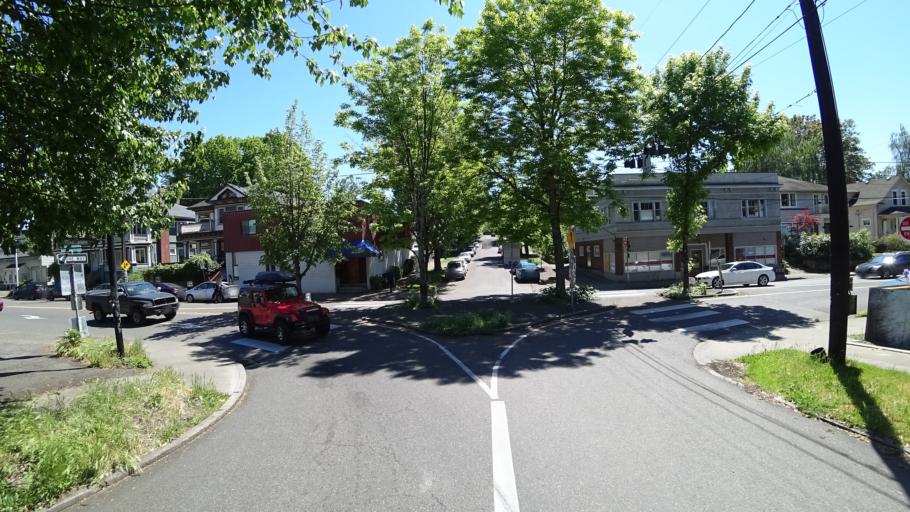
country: US
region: Oregon
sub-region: Multnomah County
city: Portland
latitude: 45.5166
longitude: -122.6402
